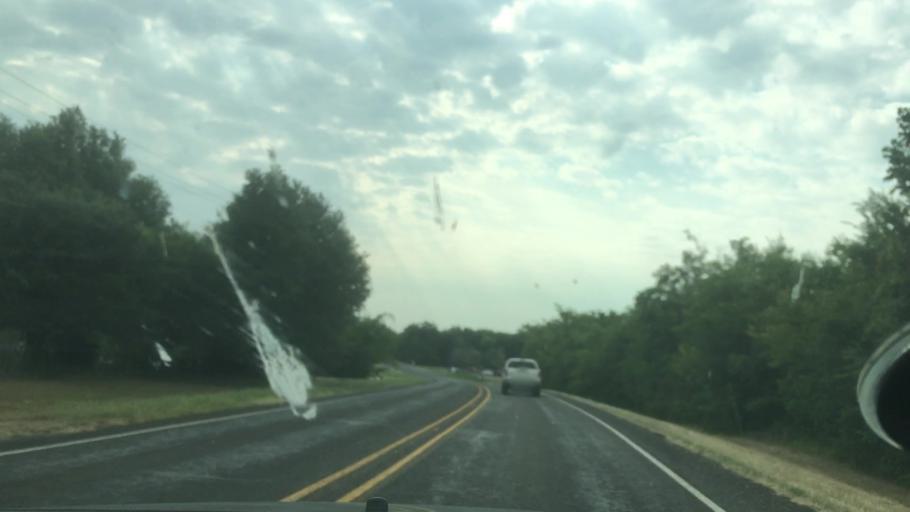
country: US
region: Texas
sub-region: Grayson County
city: Pottsboro
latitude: 33.7870
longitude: -96.6034
